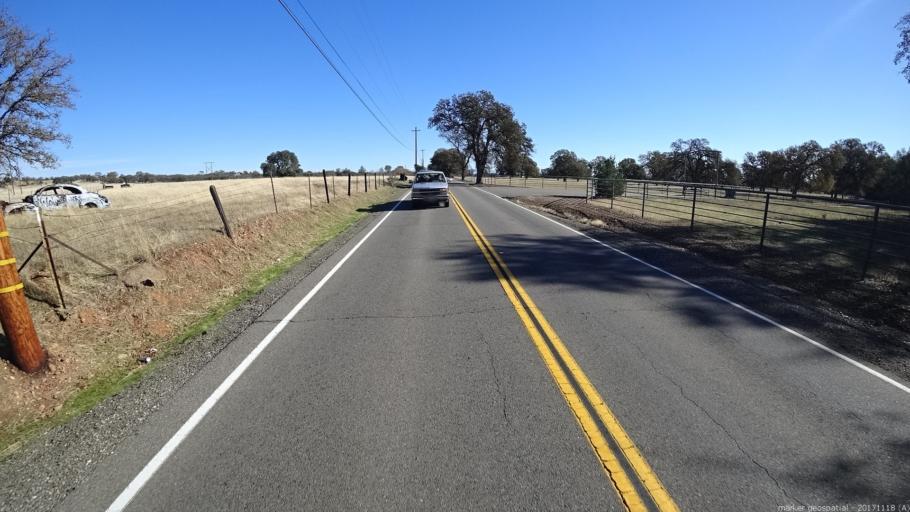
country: US
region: California
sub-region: Shasta County
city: Cottonwood
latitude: 40.3887
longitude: -122.3708
